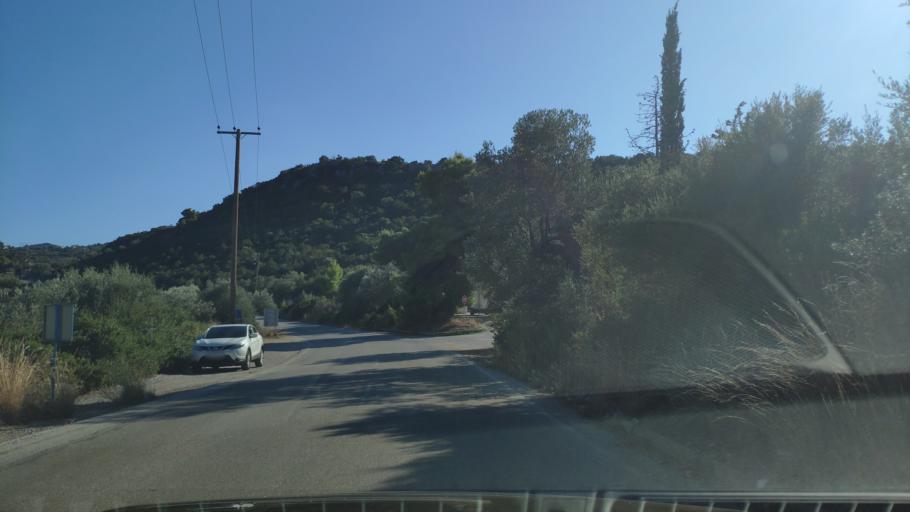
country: GR
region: Attica
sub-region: Nomos Piraios
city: Galatas
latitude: 37.5599
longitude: 23.3647
